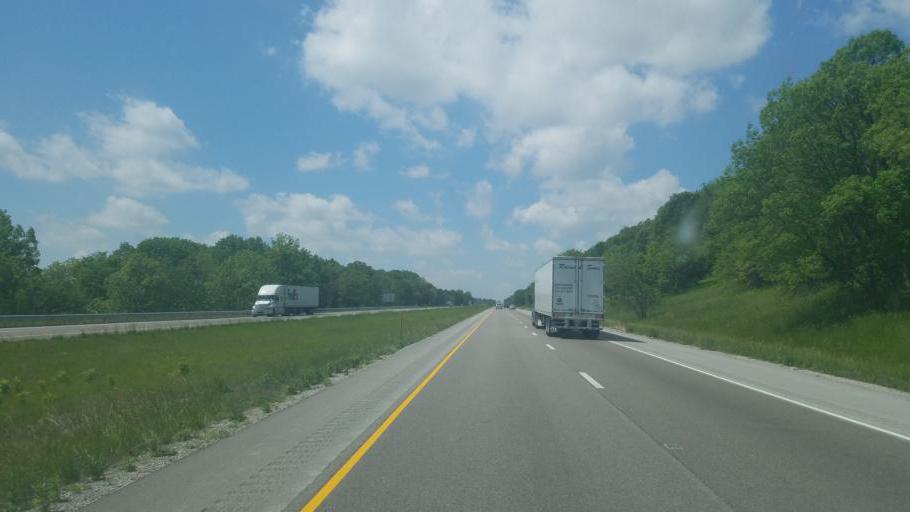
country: US
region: Illinois
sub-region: Cumberland County
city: Greenup
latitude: 39.2482
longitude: -88.1851
